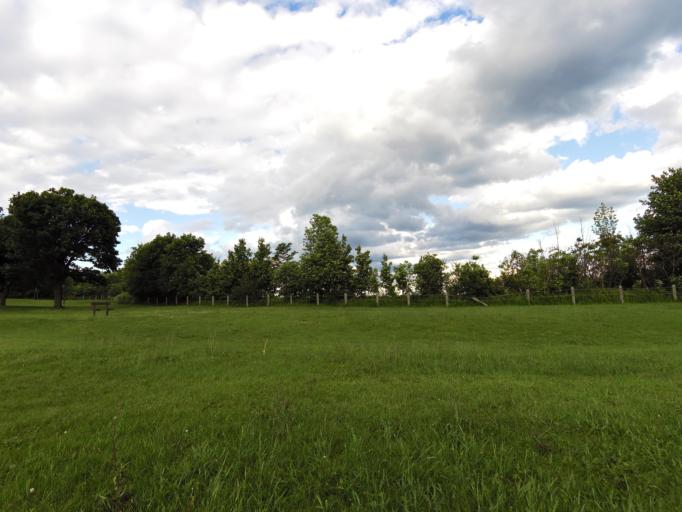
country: CA
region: Ontario
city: Scarborough
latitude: 43.7180
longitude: -79.2283
